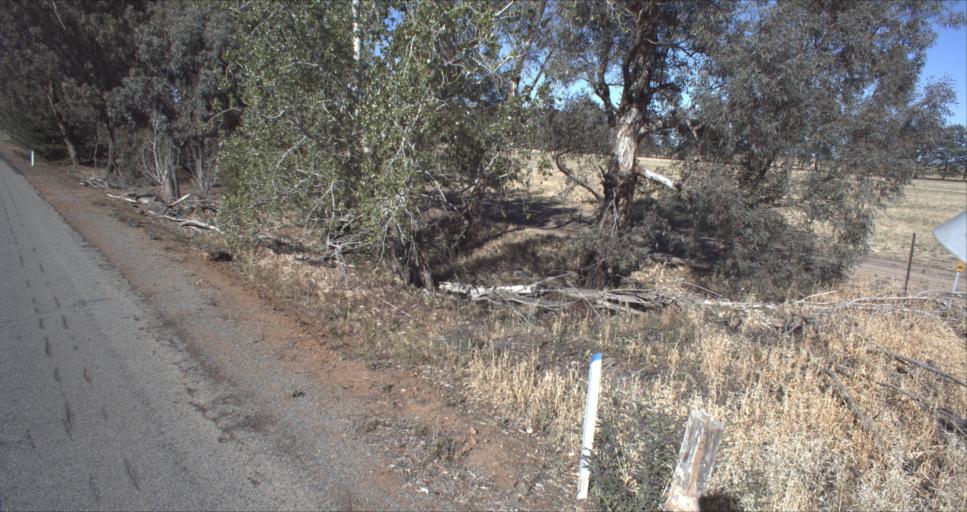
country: AU
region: New South Wales
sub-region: Leeton
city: Leeton
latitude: -34.5730
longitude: 146.3102
